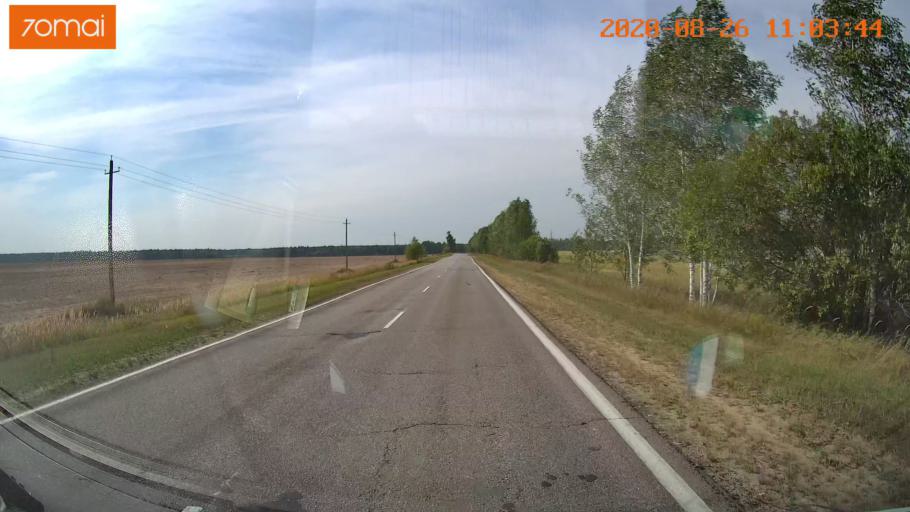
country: RU
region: Rjazan
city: Izhevskoye
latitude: 54.5377
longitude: 41.2071
